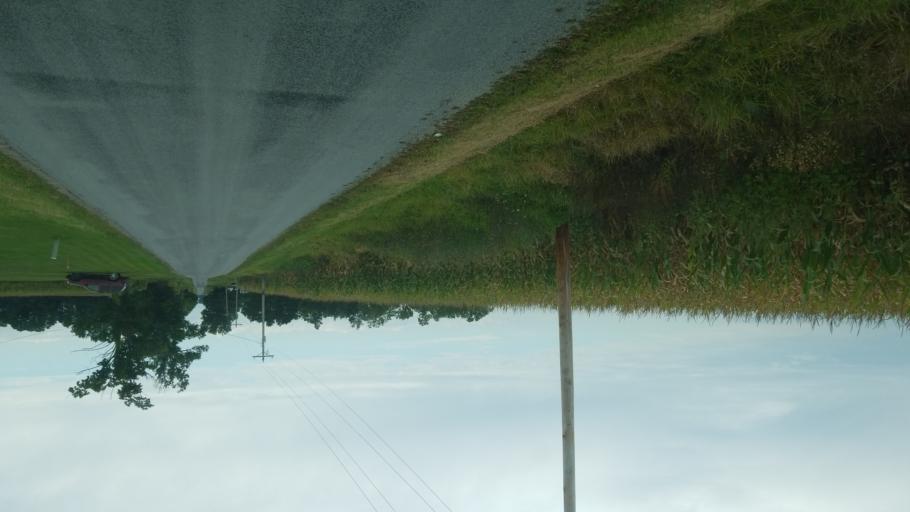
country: US
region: Ohio
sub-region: Wyandot County
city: Upper Sandusky
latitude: 40.8935
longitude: -83.1893
